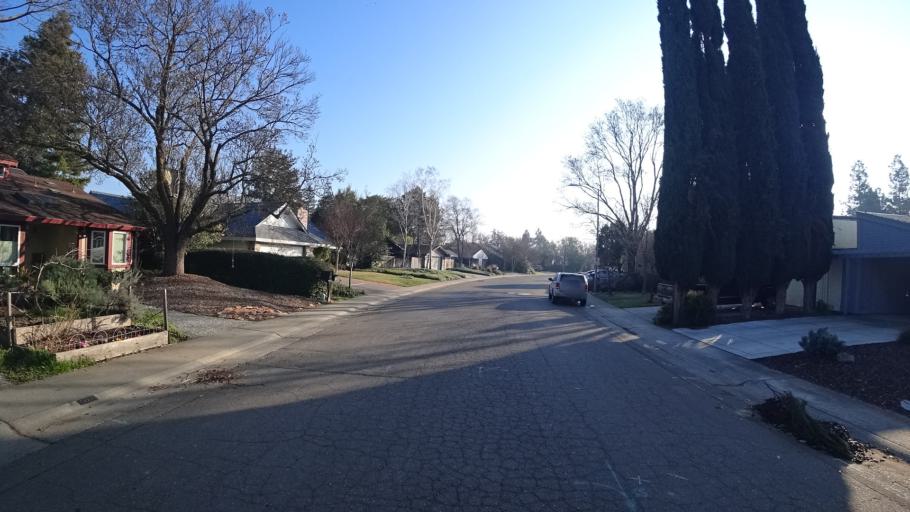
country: US
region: California
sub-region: Yolo County
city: Davis
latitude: 38.5573
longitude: -121.7908
